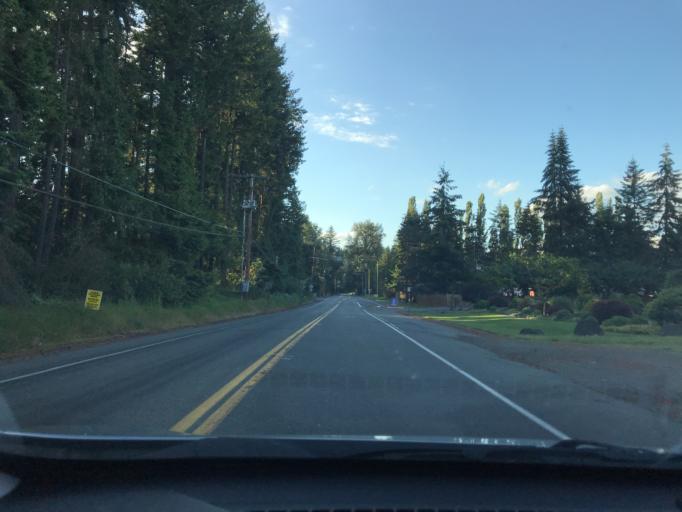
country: US
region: Washington
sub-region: King County
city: Lake Morton-Berrydale
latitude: 47.3013
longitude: -122.0865
